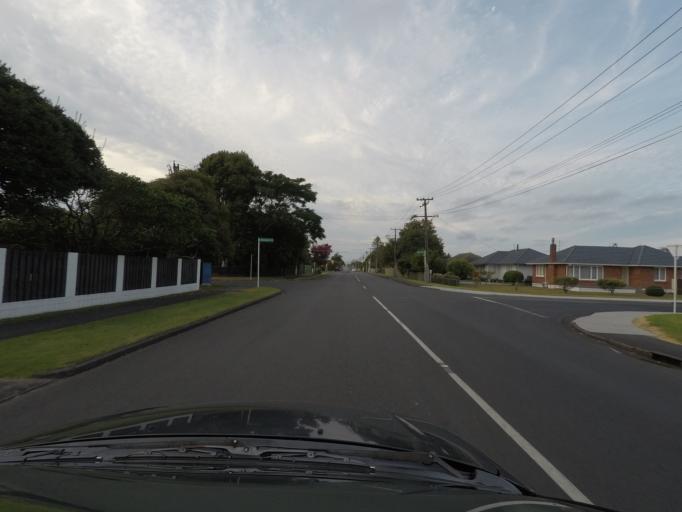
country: NZ
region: Auckland
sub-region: Auckland
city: Rosebank
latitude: -36.8391
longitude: 174.6512
